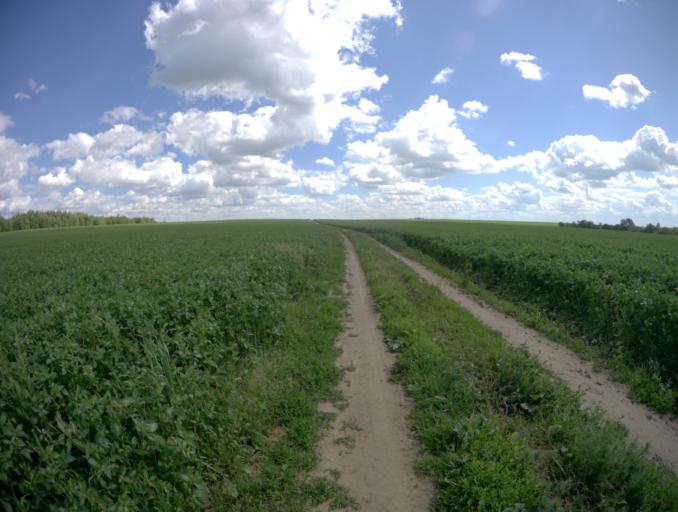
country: RU
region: Vladimir
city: Suzdal'
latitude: 56.4366
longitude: 40.2739
